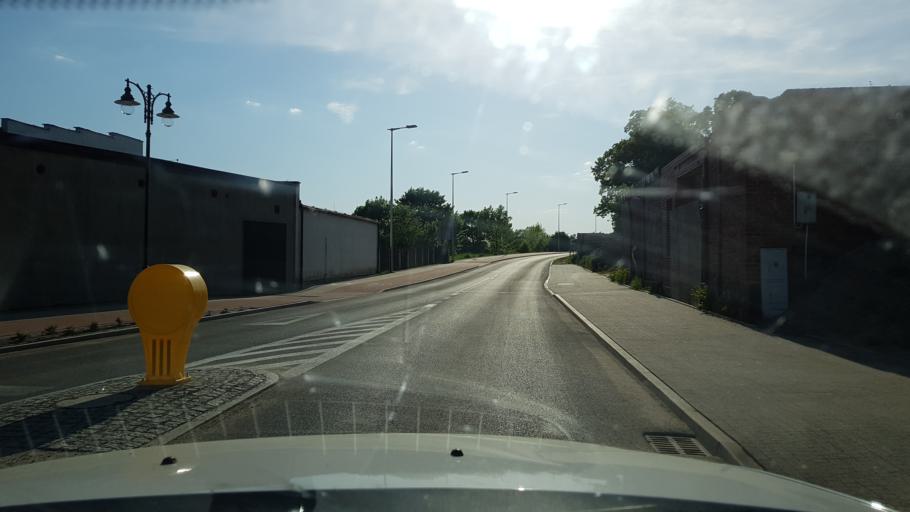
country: PL
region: West Pomeranian Voivodeship
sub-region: Powiat lobeski
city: Resko
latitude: 53.7755
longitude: 15.4062
